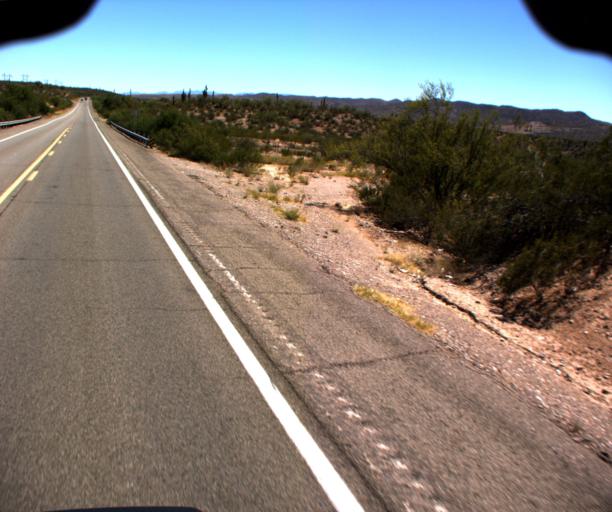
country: US
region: Arizona
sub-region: Pinal County
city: Mammoth
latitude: 32.8662
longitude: -110.7100
